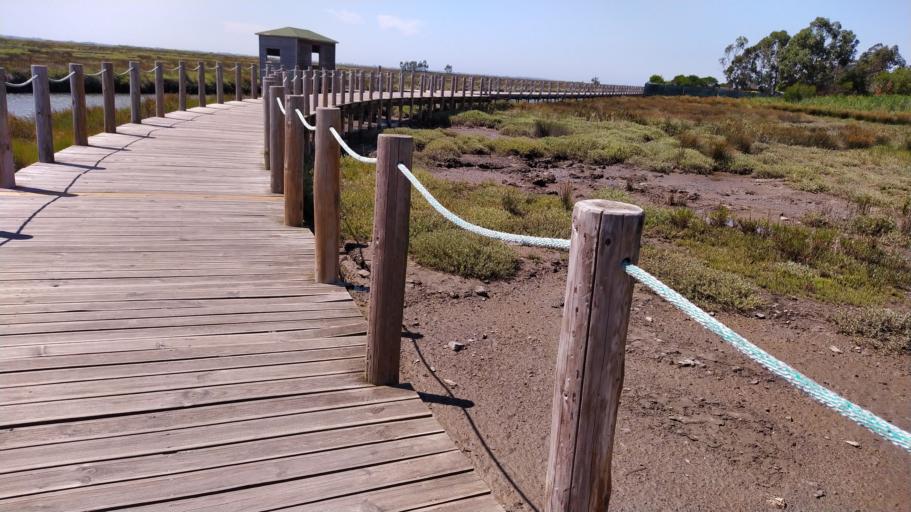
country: PT
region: Aveiro
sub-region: Aveiro
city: Aveiro
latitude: 40.6574
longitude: -8.6370
